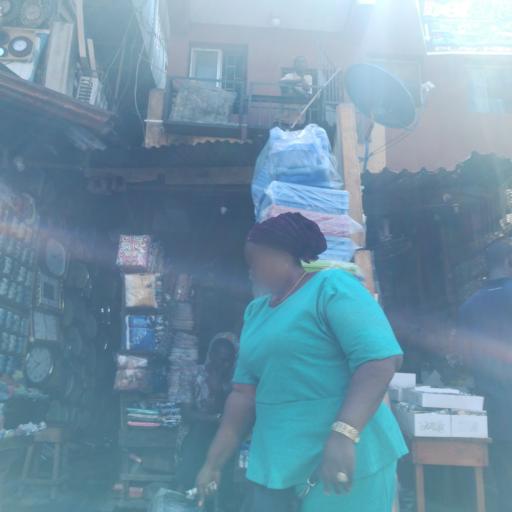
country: NG
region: Lagos
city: Lagos
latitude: 6.4595
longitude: 3.3898
